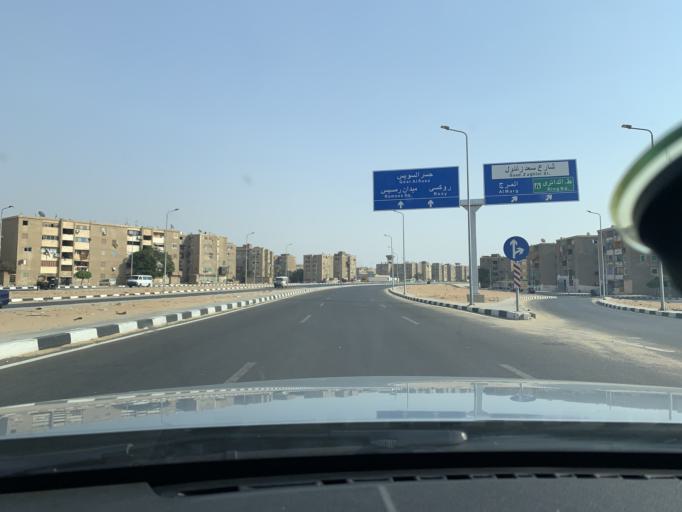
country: EG
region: Muhafazat al Qalyubiyah
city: Al Khankah
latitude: 30.1752
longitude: 31.4148
